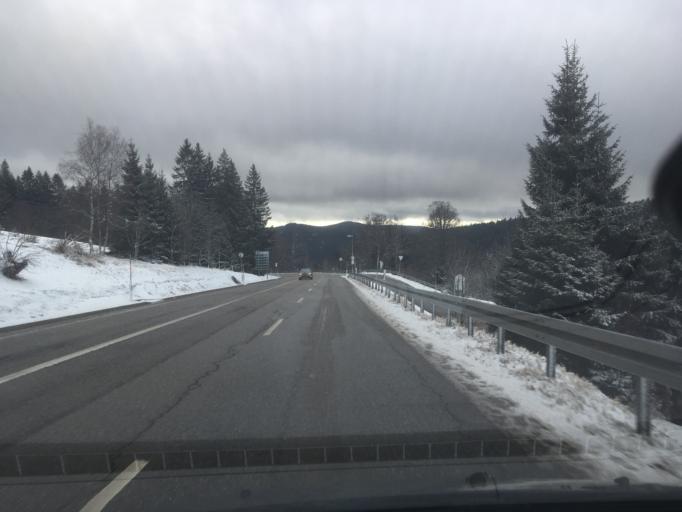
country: DE
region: Baden-Wuerttemberg
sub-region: Freiburg Region
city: Bernau
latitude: 47.8575
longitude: 8.0387
